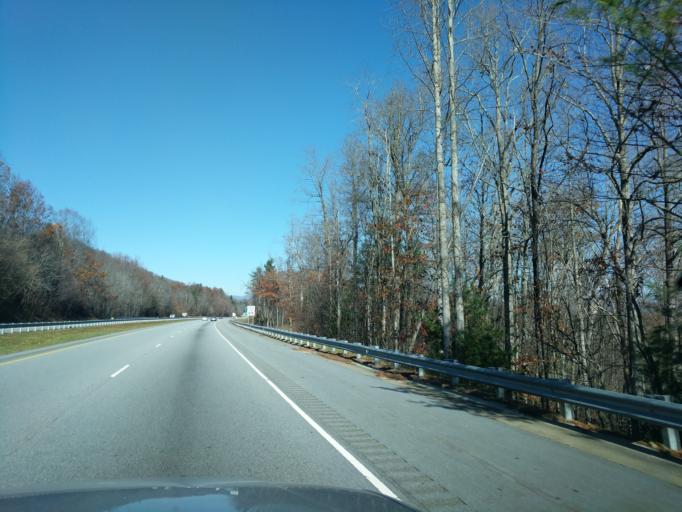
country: US
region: North Carolina
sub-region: Henderson County
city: East Flat Rock
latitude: 35.2442
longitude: -82.4120
